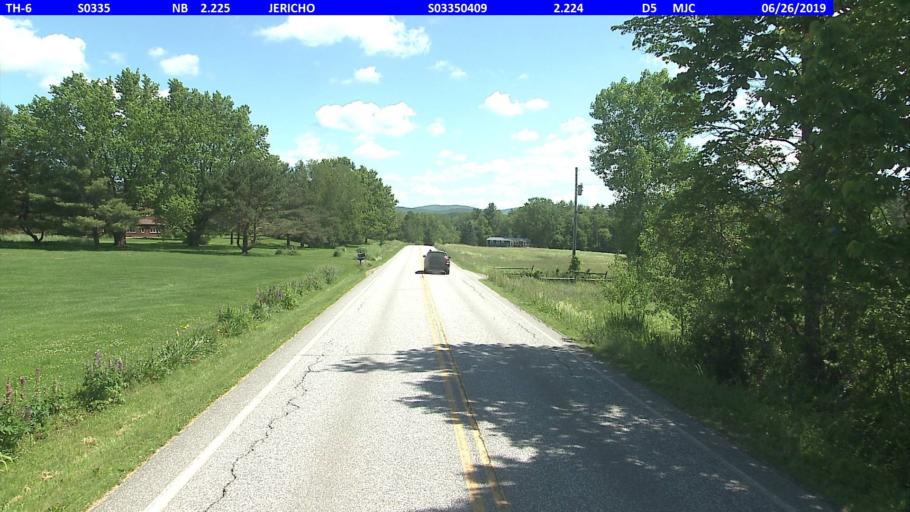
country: US
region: Vermont
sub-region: Chittenden County
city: Jericho
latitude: 44.4933
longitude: -73.0052
